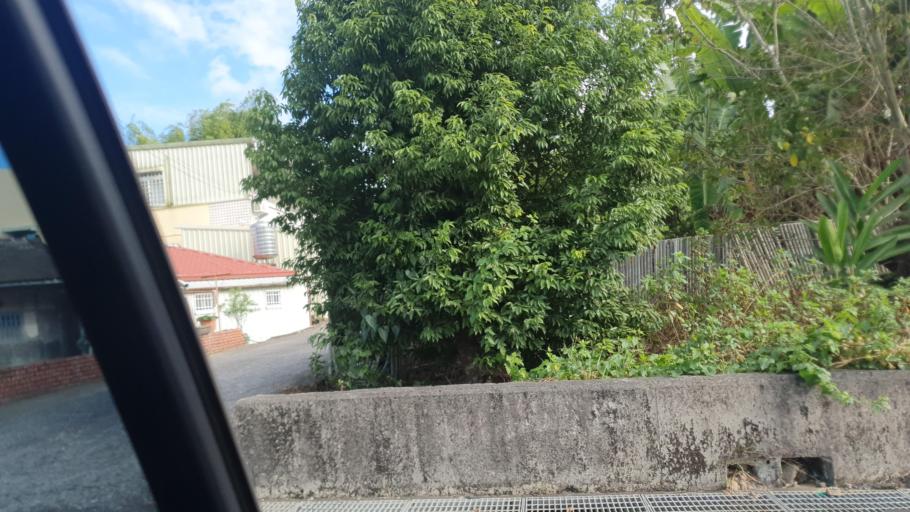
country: TW
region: Taiwan
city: Yujing
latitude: 23.0389
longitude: 120.4211
